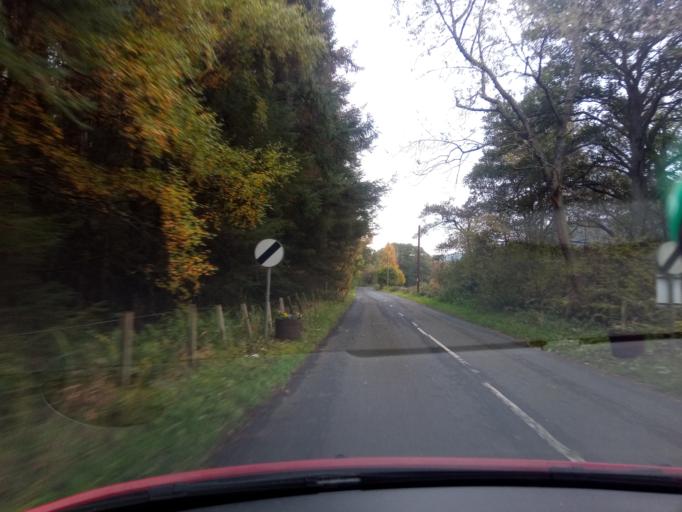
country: GB
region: Scotland
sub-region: The Scottish Borders
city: Galashiels
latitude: 55.6155
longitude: -2.8769
